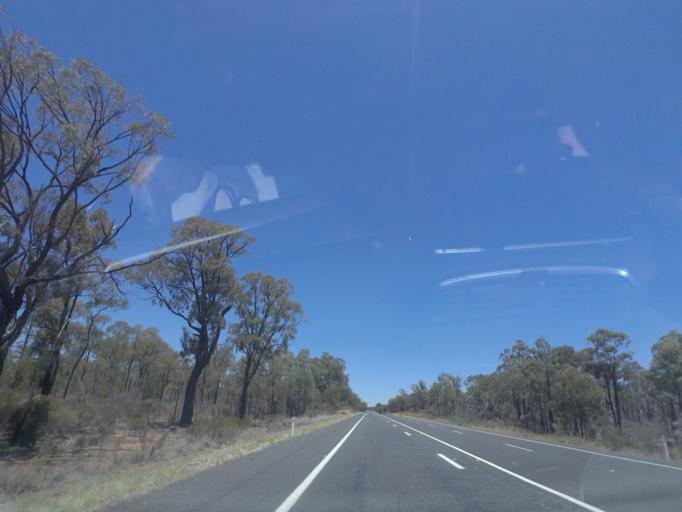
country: AU
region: New South Wales
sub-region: Warrumbungle Shire
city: Coonabarabran
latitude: -30.8755
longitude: 149.4484
